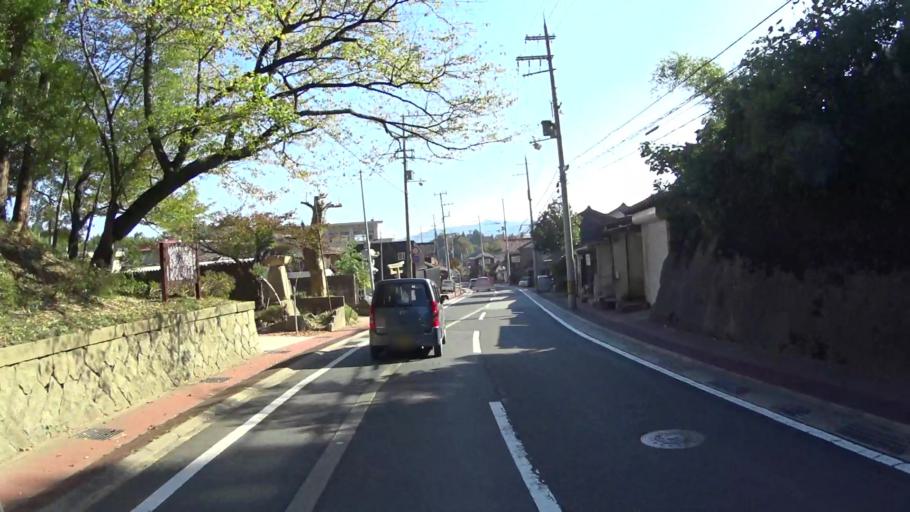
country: JP
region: Kyoto
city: Miyazu
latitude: 35.6307
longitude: 135.0552
